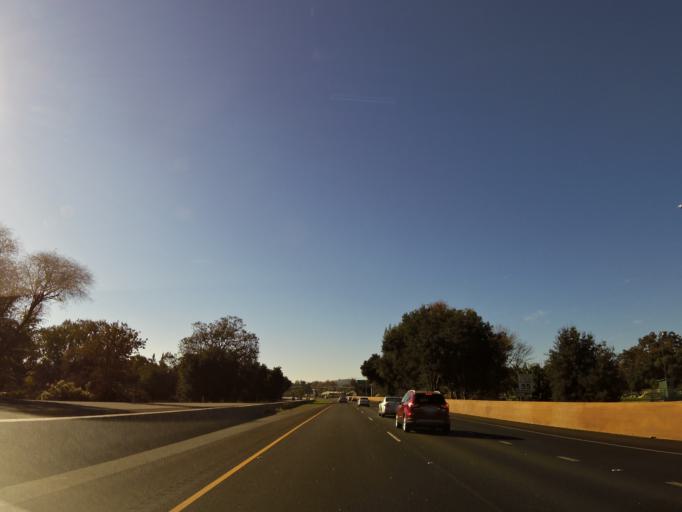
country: US
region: California
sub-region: San Luis Obispo County
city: Paso Robles
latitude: 35.6359
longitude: -120.6847
